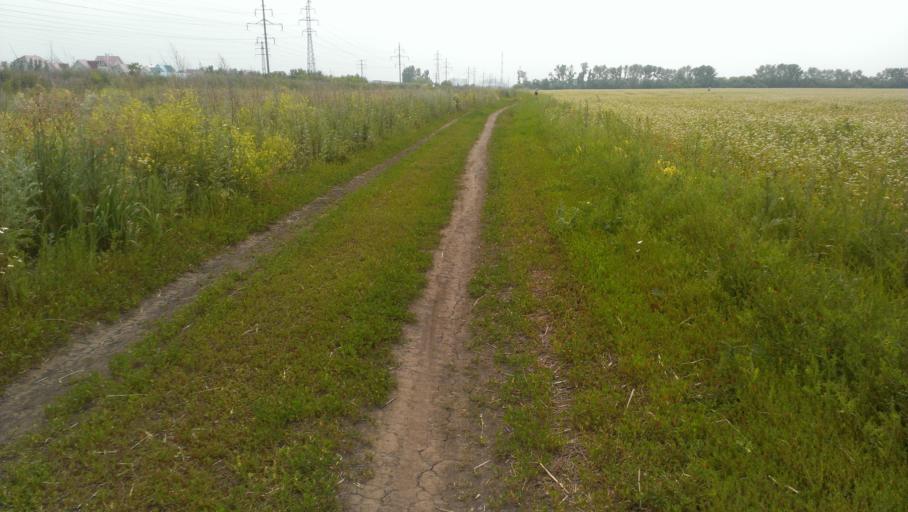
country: RU
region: Altai Krai
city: Novosilikatnyy
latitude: 53.3726
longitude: 83.6488
